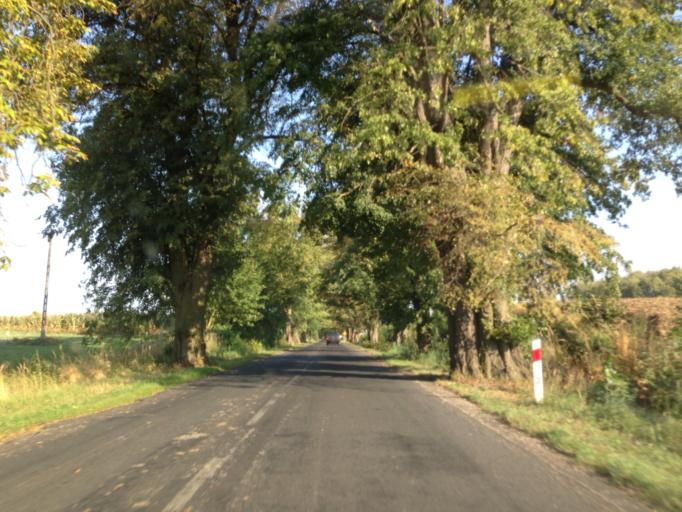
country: PL
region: Kujawsko-Pomorskie
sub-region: Powiat grudziadzki
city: Lasin
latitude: 53.5022
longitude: 19.1885
